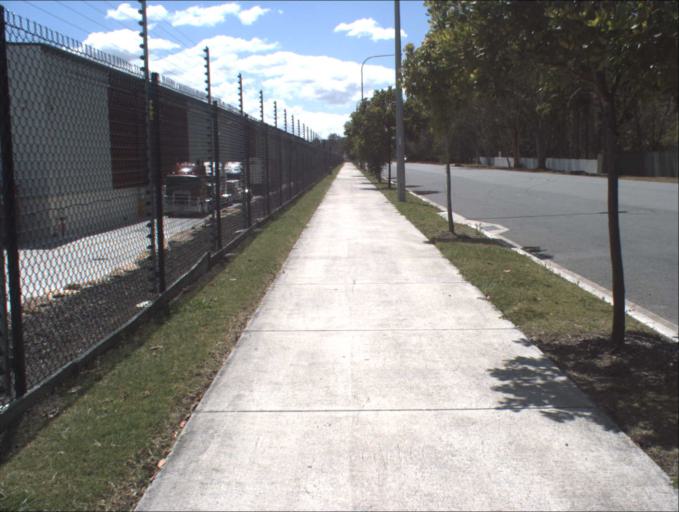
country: AU
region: Queensland
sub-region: Logan
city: Woodridge
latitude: -27.6508
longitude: 153.0917
